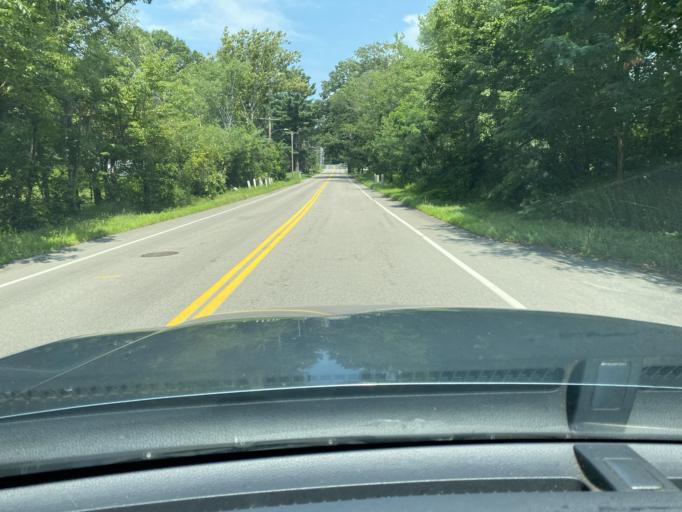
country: US
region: Massachusetts
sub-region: Norfolk County
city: Medway
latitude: 42.1591
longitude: -71.4274
